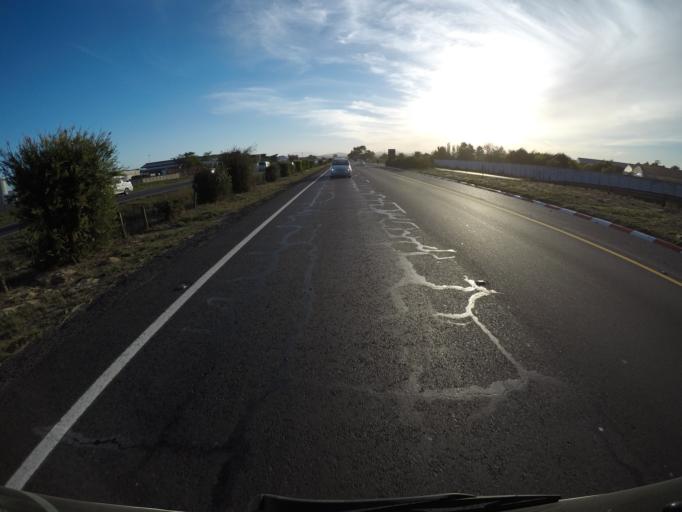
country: ZA
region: Western Cape
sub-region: City of Cape Town
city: Kraaifontein
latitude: -33.8360
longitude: 18.7333
